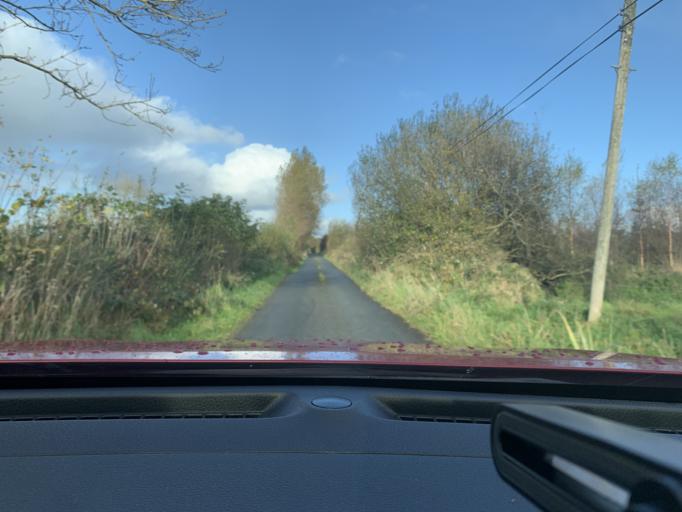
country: IE
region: Connaught
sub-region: Sligo
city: Ballymote
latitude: 54.0956
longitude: -8.4383
